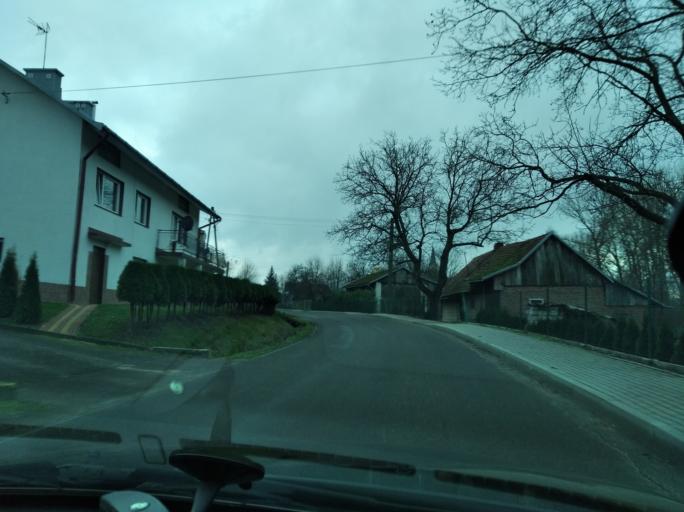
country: PL
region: Subcarpathian Voivodeship
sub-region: Powiat przeworski
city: Sietesz
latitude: 49.9985
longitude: 22.3554
